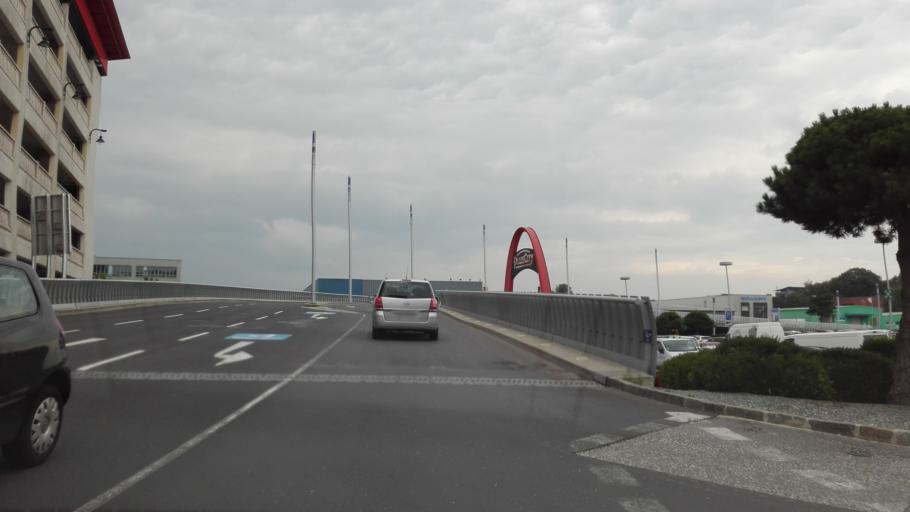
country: AT
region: Upper Austria
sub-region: Politischer Bezirk Linz-Land
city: Traun
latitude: 48.2438
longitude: 14.2341
